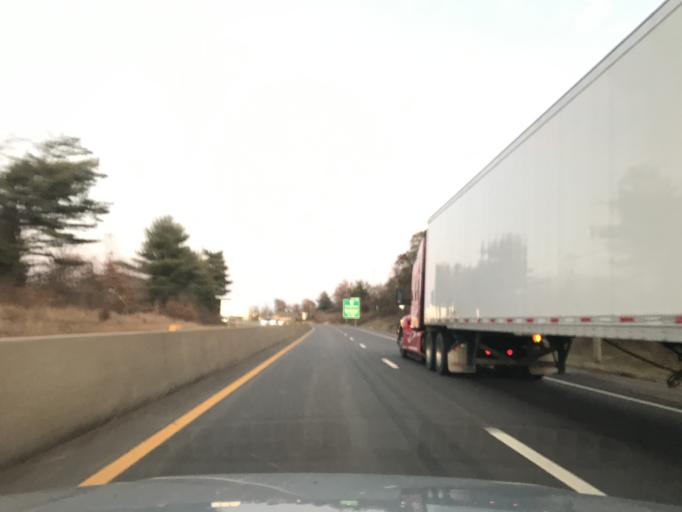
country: US
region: Missouri
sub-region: Marion County
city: Hannibal
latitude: 39.7148
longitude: -91.3866
